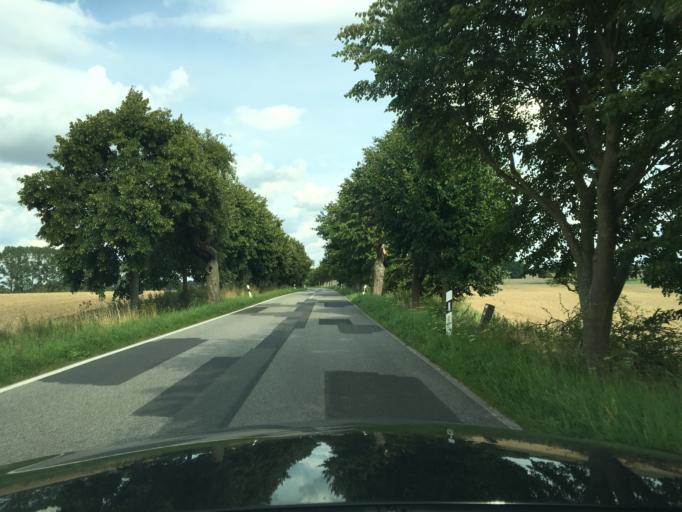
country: DE
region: Mecklenburg-Vorpommern
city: Mollenhagen
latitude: 53.4802
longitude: 12.9748
